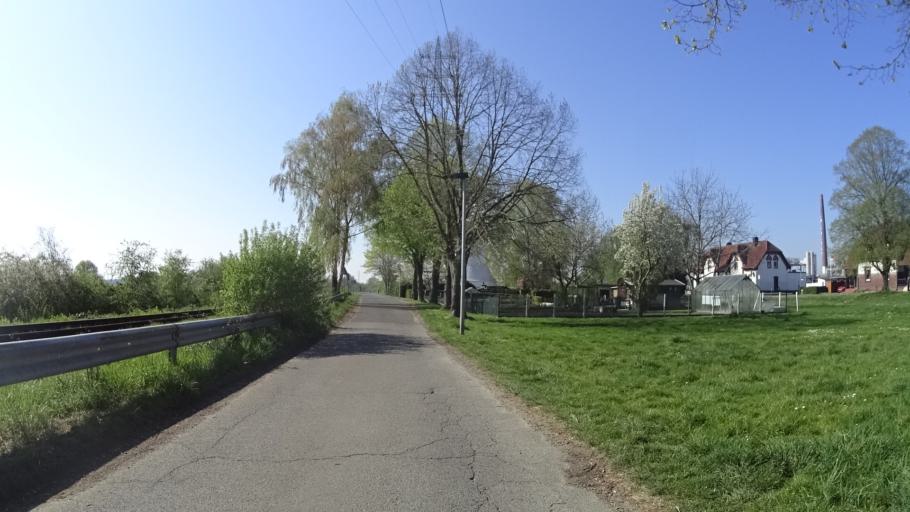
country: DE
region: North Rhine-Westphalia
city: Rheinberg
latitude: 51.5674
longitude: 6.5881
